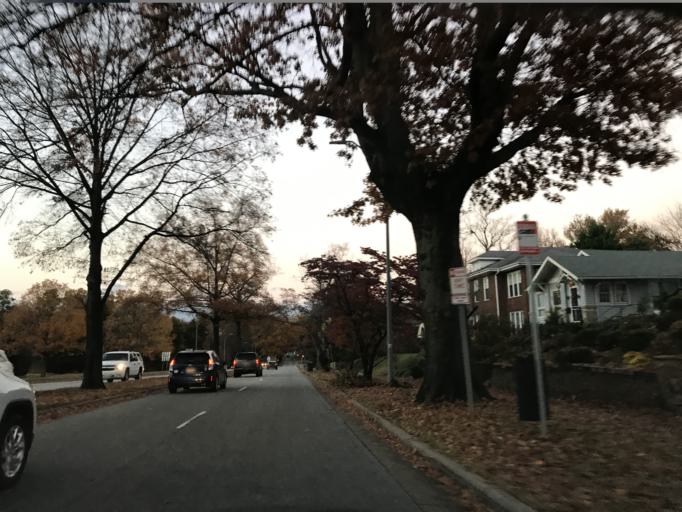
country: US
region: North Carolina
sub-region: Wake County
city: West Raleigh
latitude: 35.7966
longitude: -78.6463
